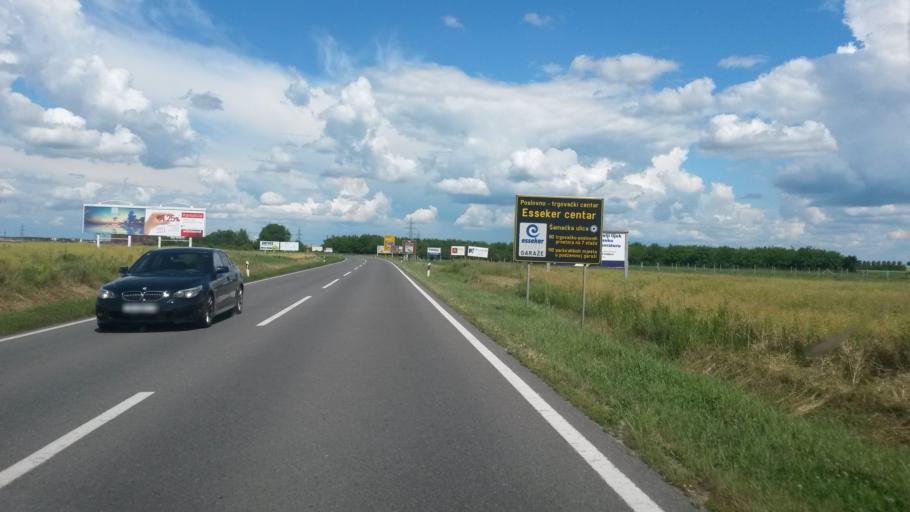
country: HR
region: Osjecko-Baranjska
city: Visnjevac
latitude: 45.5491
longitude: 18.6245
